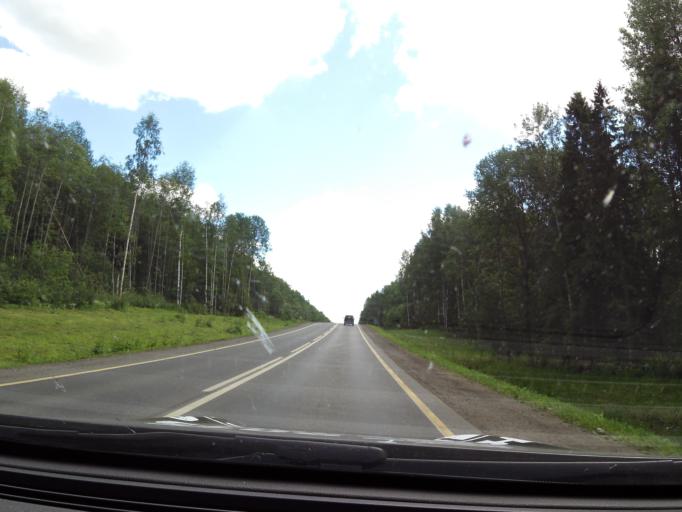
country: RU
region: Vologda
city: Molochnoye
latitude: 59.2736
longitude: 39.7210
